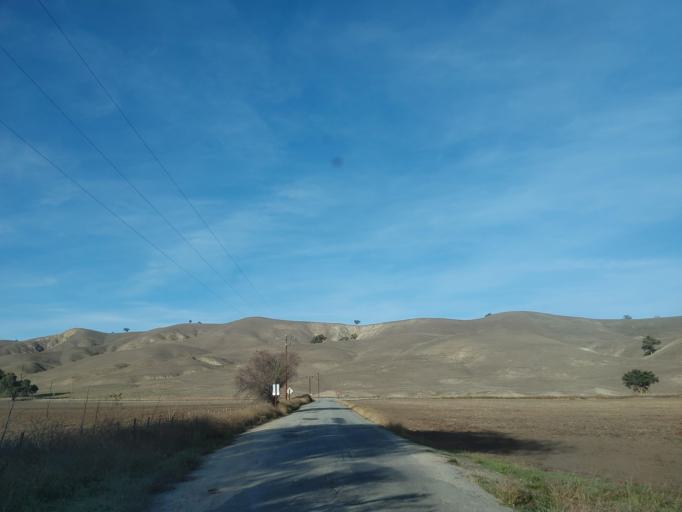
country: US
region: California
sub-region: San Benito County
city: Ridgemark
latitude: 36.7056
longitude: -121.3287
